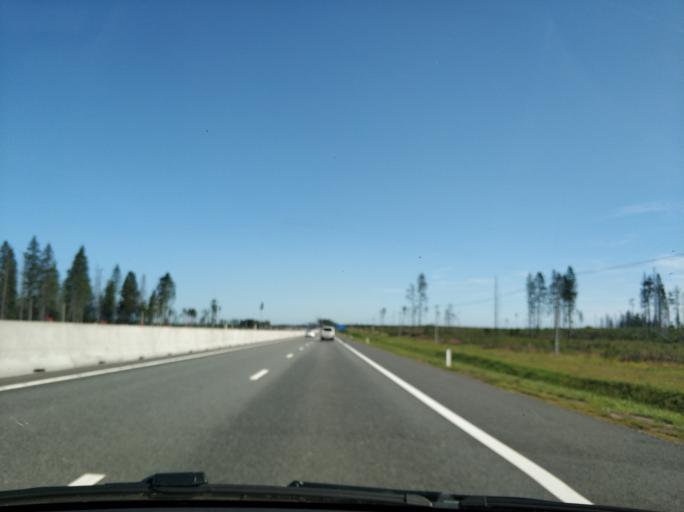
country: RU
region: Leningrad
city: Sosnovo
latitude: 60.4933
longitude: 30.1959
